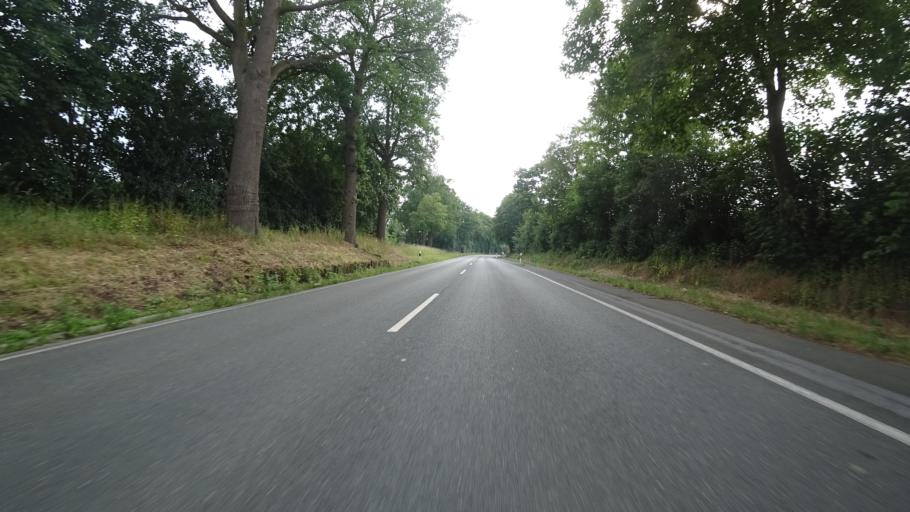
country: DE
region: North Rhine-Westphalia
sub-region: Regierungsbezirk Detmold
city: Guetersloh
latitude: 51.9540
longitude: 8.3673
